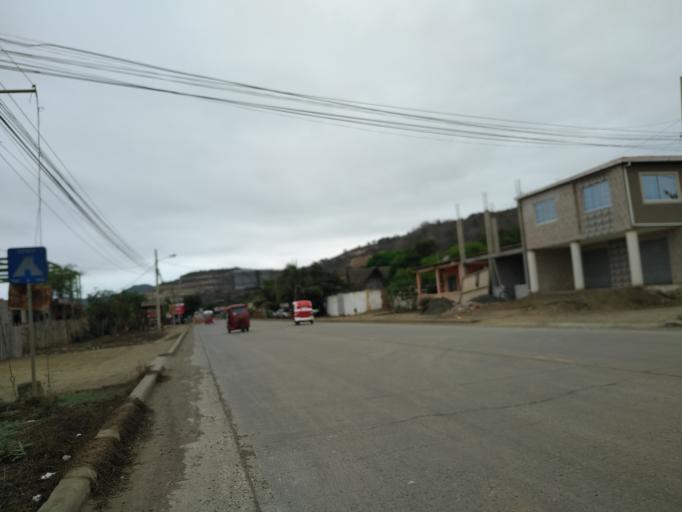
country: EC
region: Manabi
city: Jipijapa
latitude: -1.5528
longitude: -80.8077
